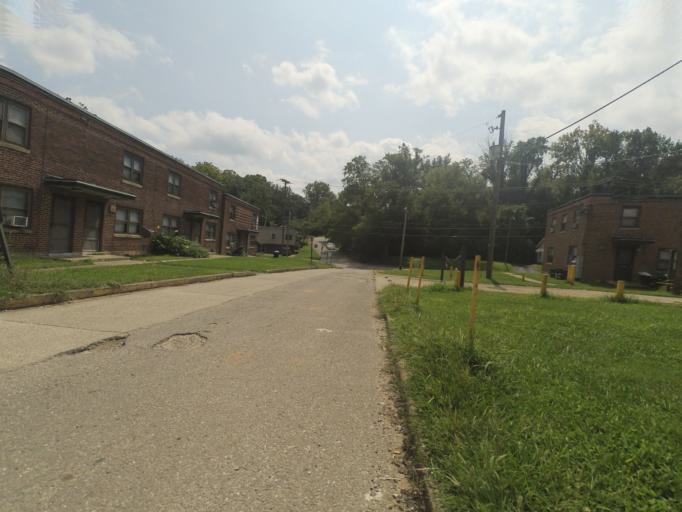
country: US
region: West Virginia
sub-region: Cabell County
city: Huntington
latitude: 38.4095
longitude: -82.4008
